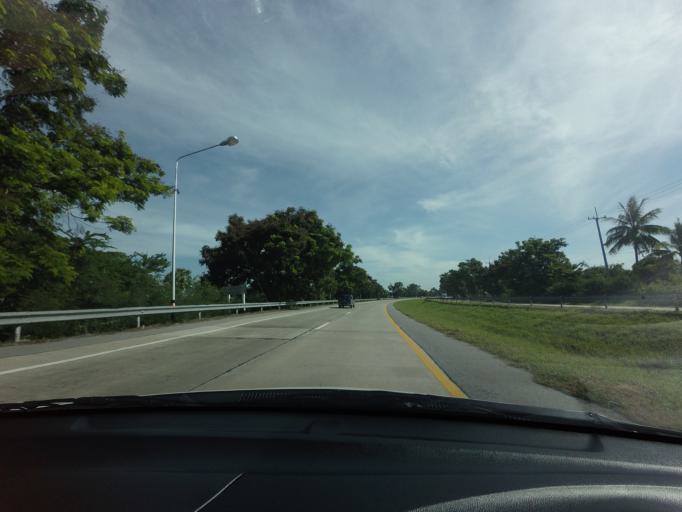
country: TH
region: Suphan Buri
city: Suphan Buri
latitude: 14.4725
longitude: 100.0393
